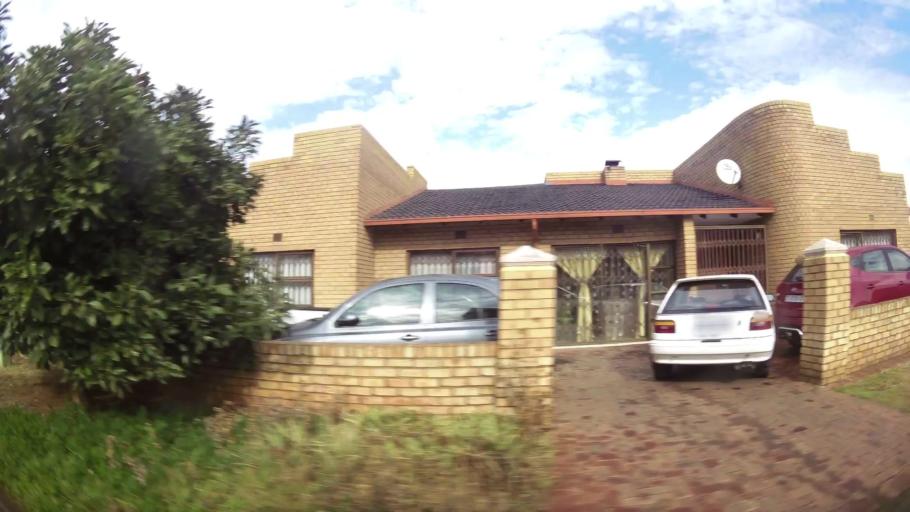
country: ZA
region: Gauteng
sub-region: Ekurhuleni Metropolitan Municipality
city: Germiston
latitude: -26.3246
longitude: 28.1872
